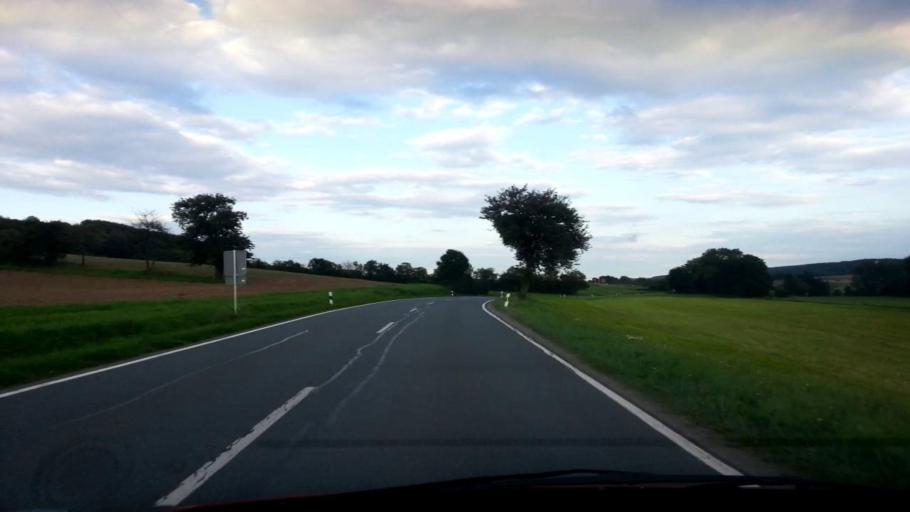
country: DE
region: Bavaria
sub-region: Regierungsbezirk Unterfranken
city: Geiselwind
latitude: 49.7726
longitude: 10.4837
